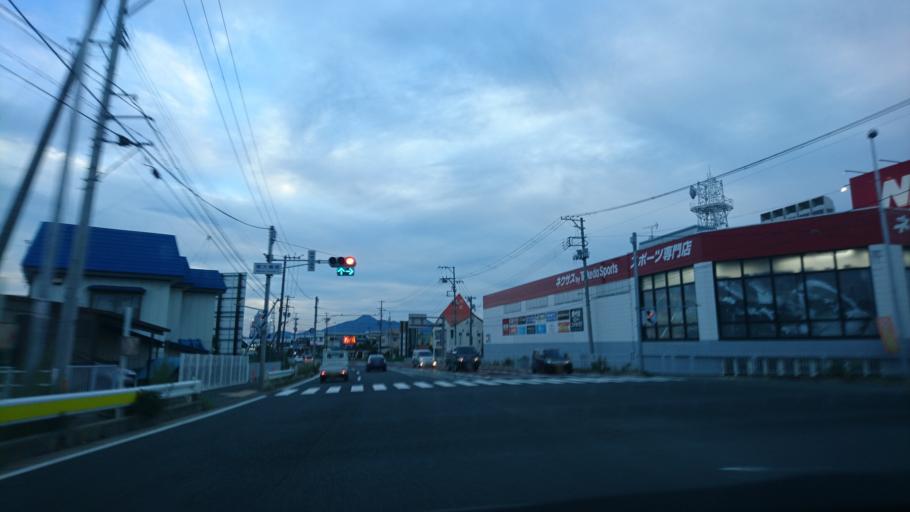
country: JP
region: Iwate
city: Morioka-shi
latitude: 39.6832
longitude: 141.1571
